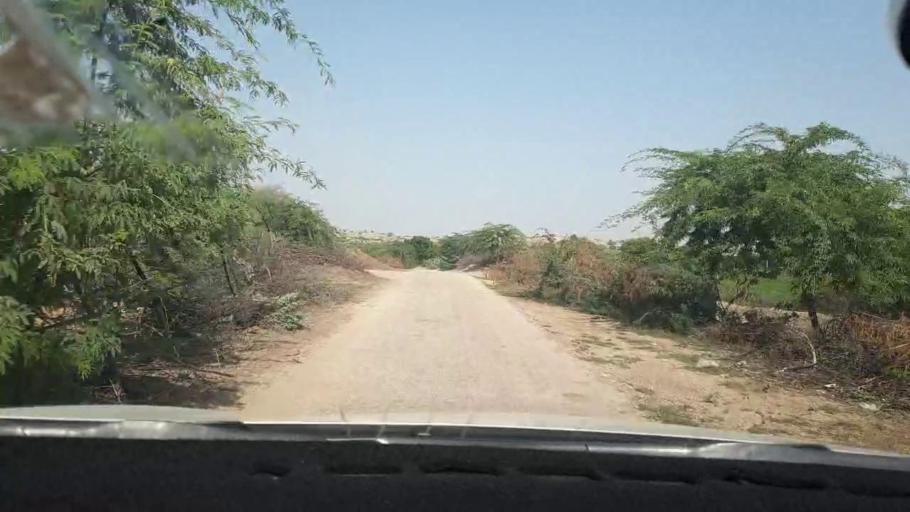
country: PK
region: Sindh
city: Tando Mittha Khan
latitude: 25.8794
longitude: 69.3881
